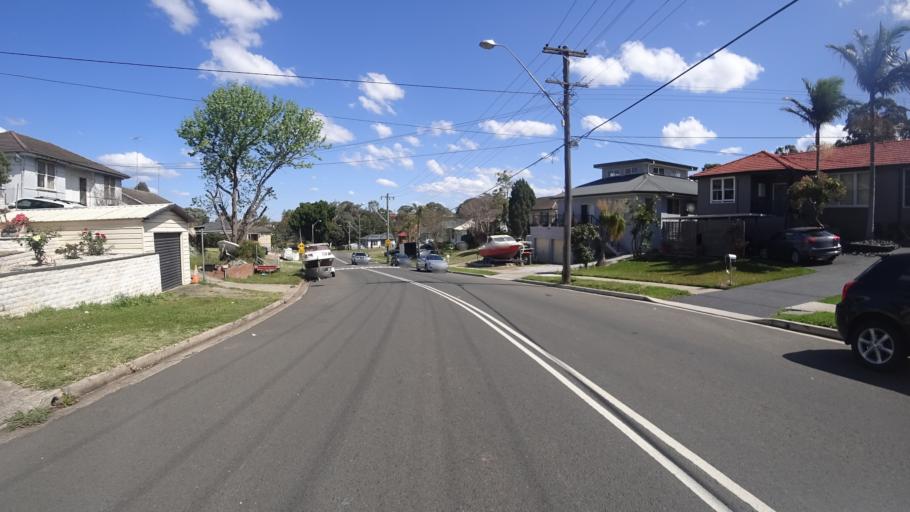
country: AU
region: New South Wales
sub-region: Fairfield
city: Cabramatta West
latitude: -33.9032
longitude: 150.9075
